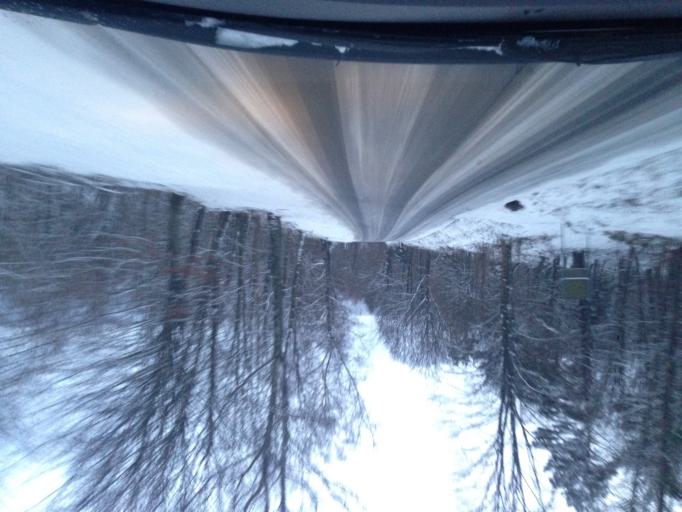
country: PL
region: Subcarpathian Voivodeship
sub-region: Powiat jasielski
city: Krempna
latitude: 49.5261
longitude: 21.5014
